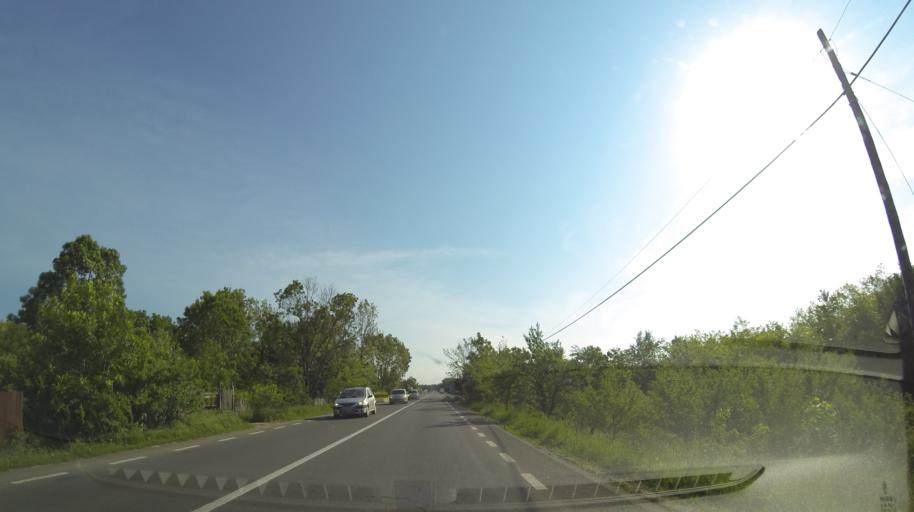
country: RO
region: Arges
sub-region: Comuna Lunca Corbului
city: Lunca Corbului
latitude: 44.6814
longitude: 24.7567
